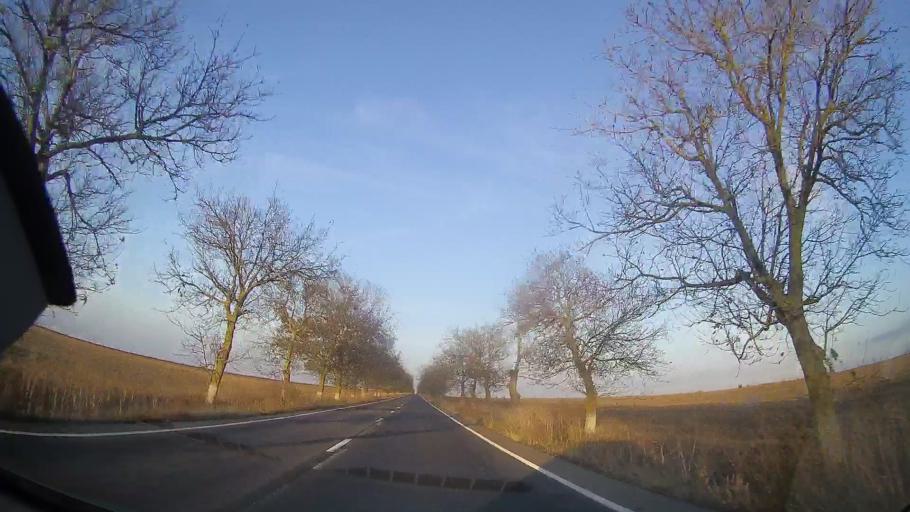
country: RO
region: Constanta
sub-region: Comuna Comana
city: Comana
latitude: 43.9083
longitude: 28.3344
